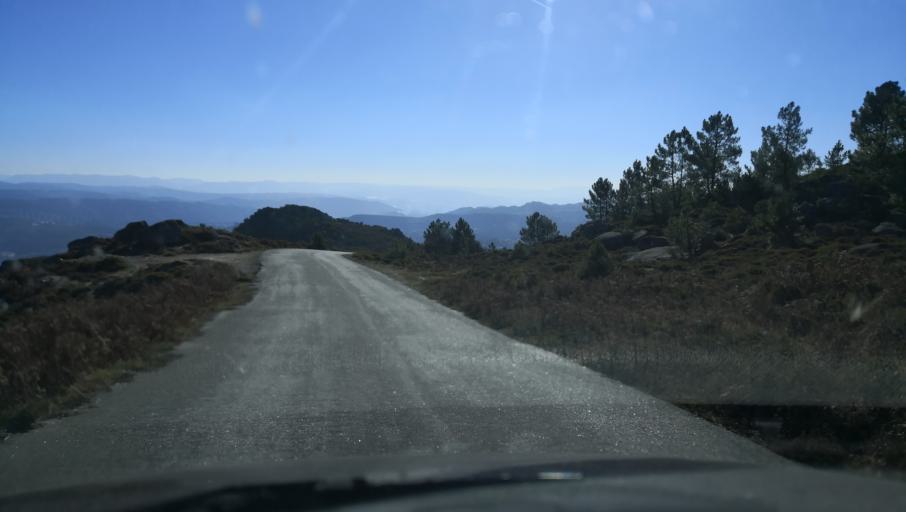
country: PT
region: Vila Real
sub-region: Vila Real
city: Vila Real
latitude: 41.3268
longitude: -7.7899
